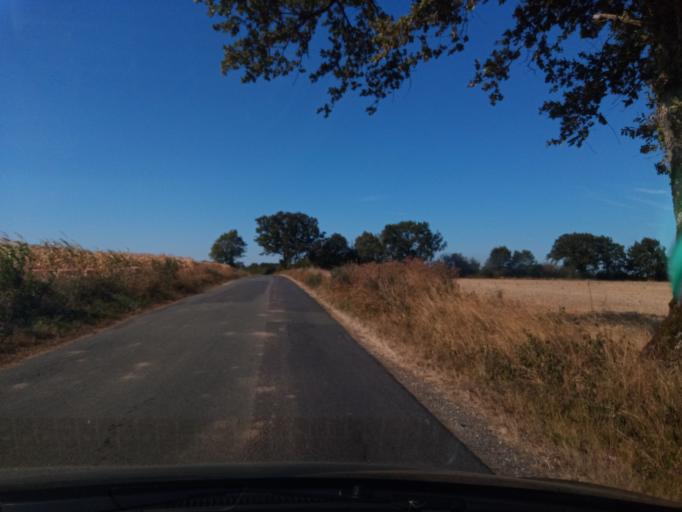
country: FR
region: Poitou-Charentes
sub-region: Departement de la Vienne
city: Montmorillon
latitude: 46.4988
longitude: 0.8085
